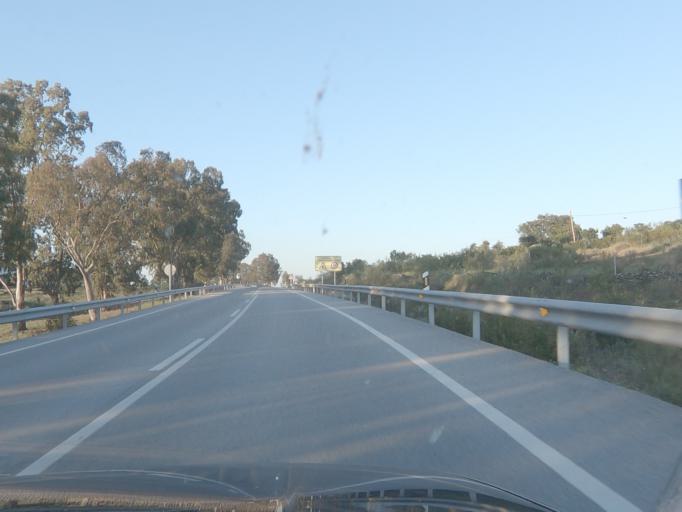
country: ES
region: Extremadura
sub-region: Provincia de Caceres
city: Valencia de Alcantara
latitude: 39.4921
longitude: -7.1948
